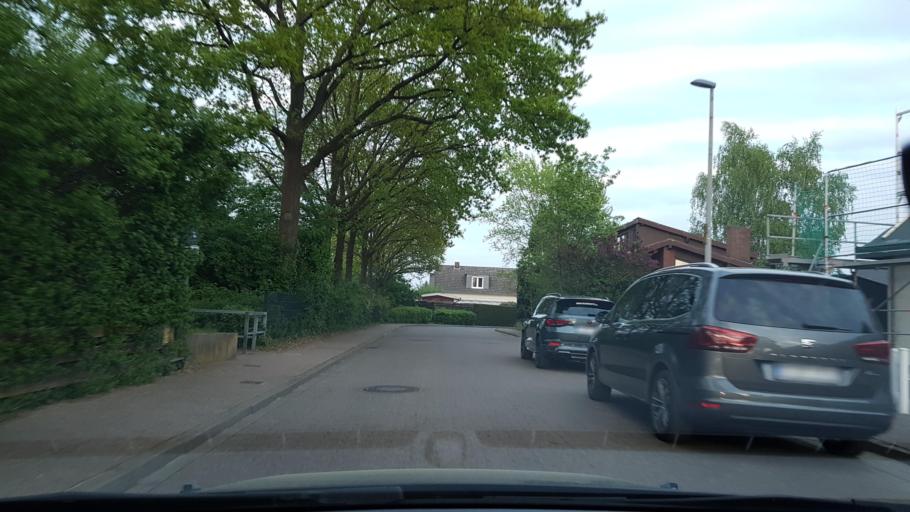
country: DE
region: Lower Saxony
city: Garbsen
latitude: 52.4381
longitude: 9.5460
